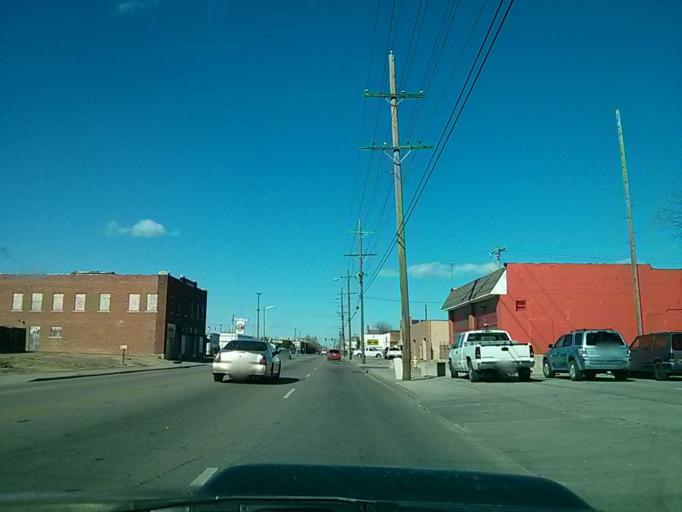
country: US
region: Oklahoma
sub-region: Tulsa County
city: Tulsa
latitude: 36.1638
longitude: -95.9581
